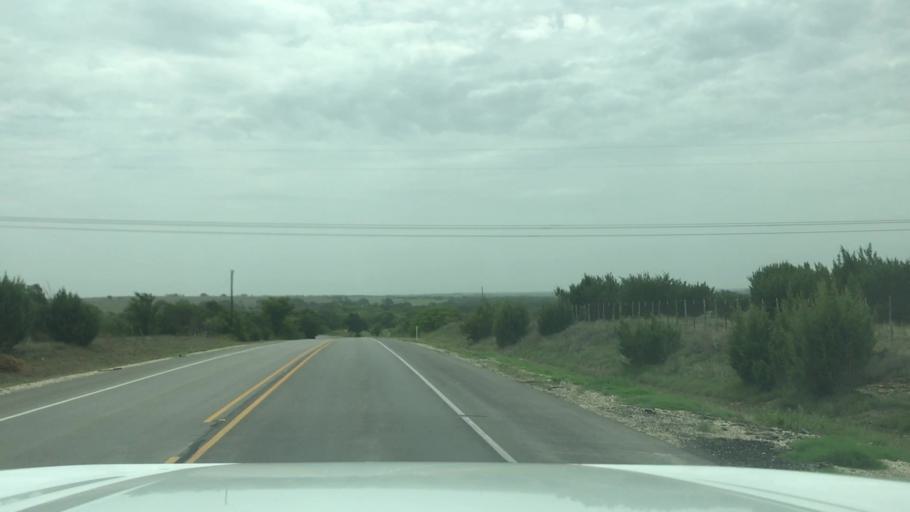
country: US
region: Texas
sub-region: Erath County
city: Dublin
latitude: 32.0766
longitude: -98.2364
